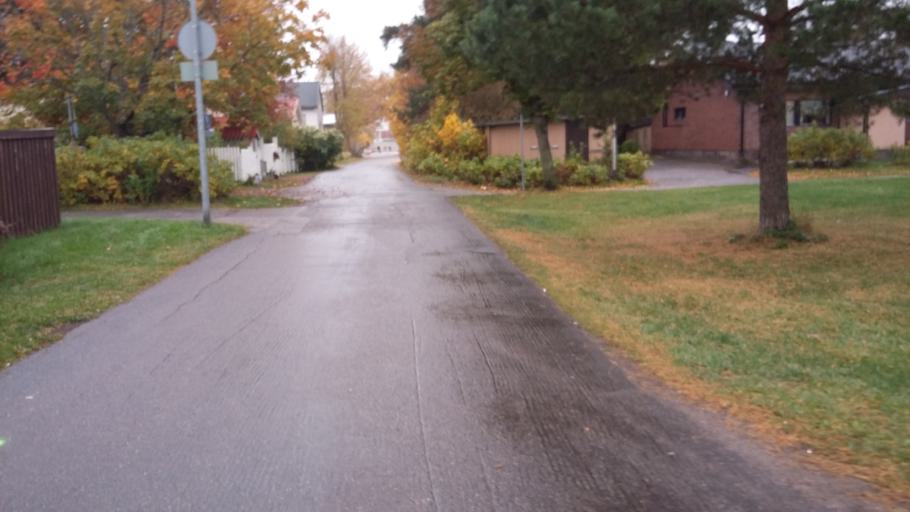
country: FI
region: Uusimaa
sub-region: Helsinki
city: Vantaa
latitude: 60.2962
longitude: 25.0289
